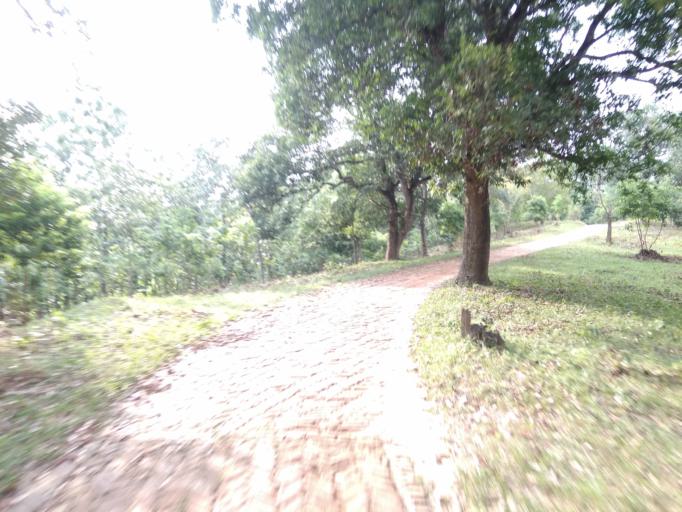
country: BD
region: Chittagong
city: Manikchari
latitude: 22.9303
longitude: 91.9119
